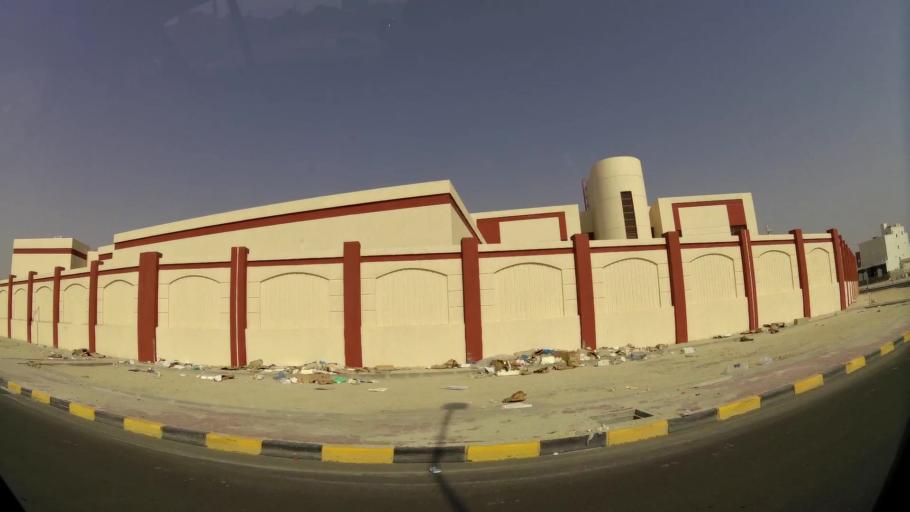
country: KW
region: Muhafazat al Jahra'
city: Al Jahra'
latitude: 29.3505
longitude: 47.7649
